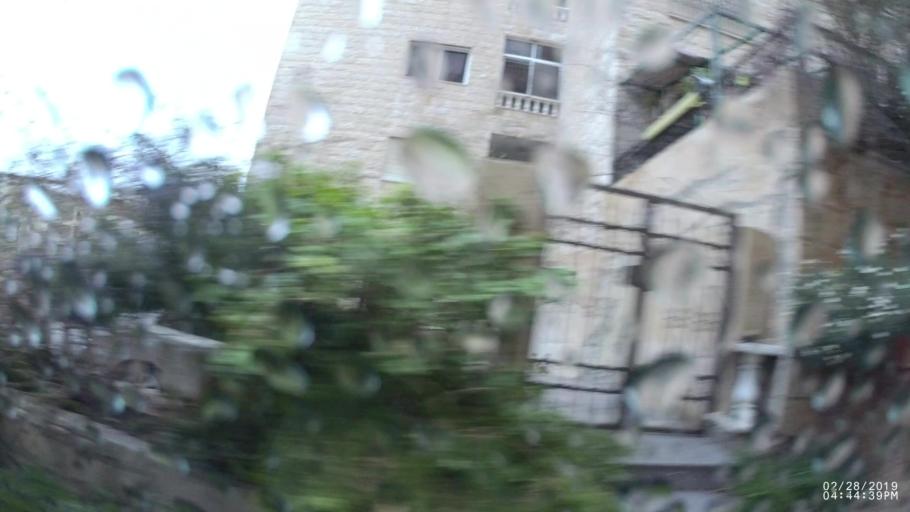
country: JO
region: Amman
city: Amman
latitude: 32.0054
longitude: 35.9312
